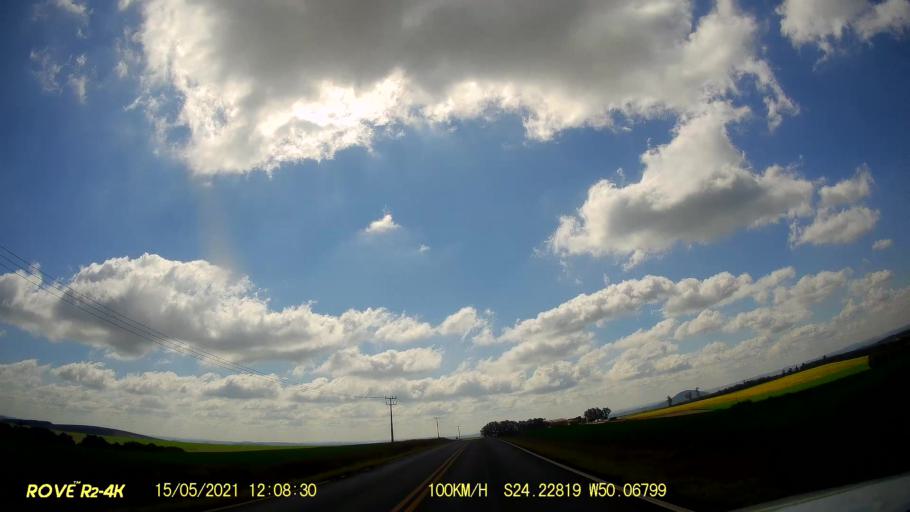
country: BR
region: Parana
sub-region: Pirai Do Sul
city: Pirai do Sul
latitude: -24.2282
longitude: -50.0678
